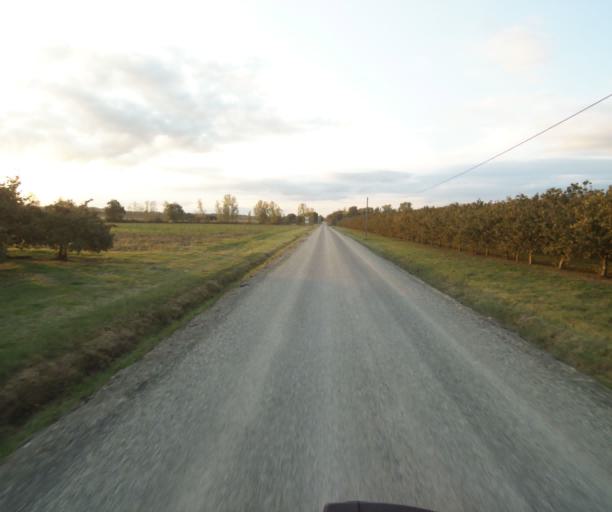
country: FR
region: Midi-Pyrenees
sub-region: Departement du Tarn-et-Garonne
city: Verdun-sur-Garonne
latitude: 43.8315
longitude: 1.2258
